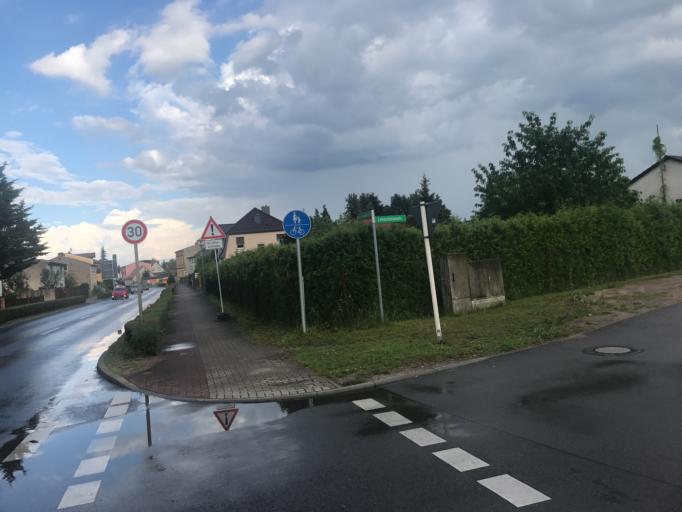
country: DE
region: Brandenburg
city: Marienwerder
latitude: 52.8508
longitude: 13.6748
